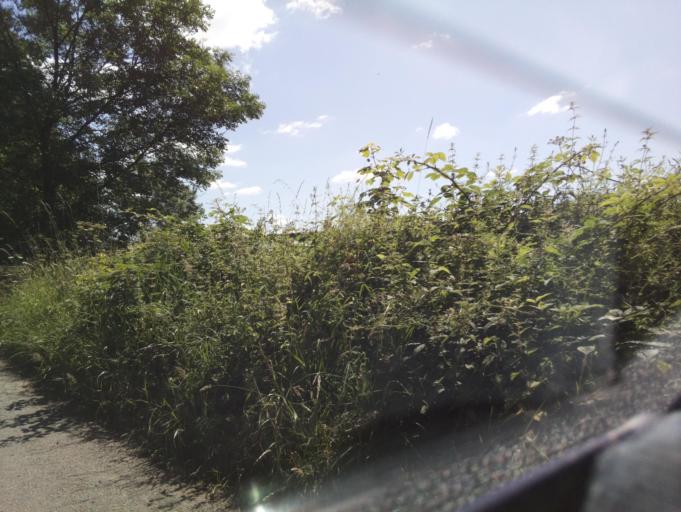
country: GB
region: England
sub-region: Derbyshire
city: Buxton
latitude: 53.1815
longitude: -1.8639
